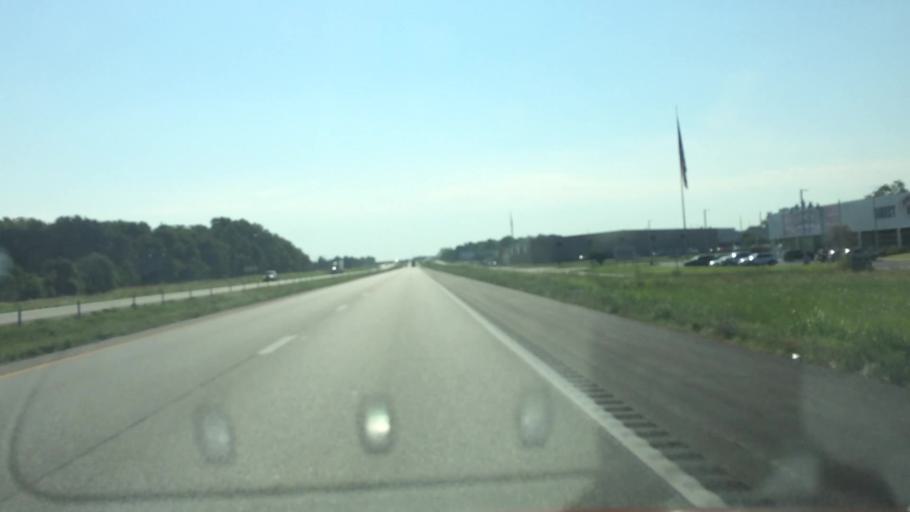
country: US
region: Missouri
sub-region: Greene County
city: Strafford
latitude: 37.2500
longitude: -93.2009
